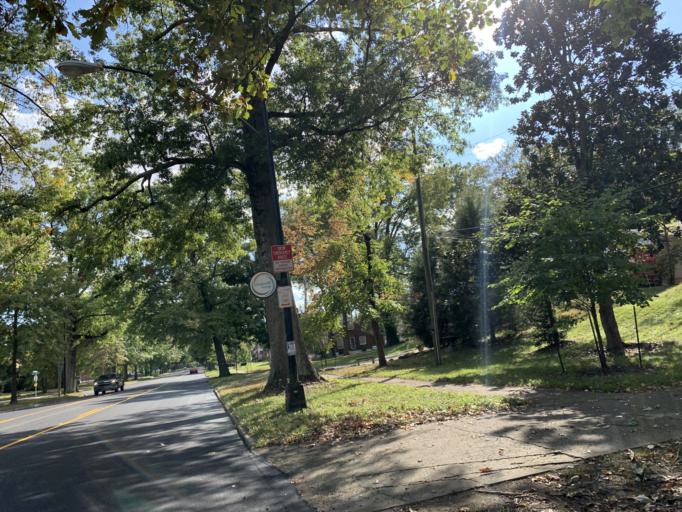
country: US
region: Indiana
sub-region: Floyd County
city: New Albany
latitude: 38.2484
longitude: -85.8296
